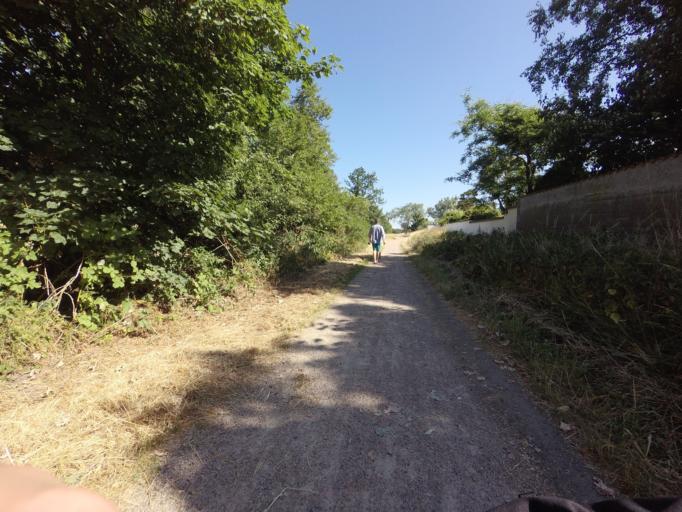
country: SE
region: Skane
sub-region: Vellinge Kommun
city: Skanor med Falsterbo
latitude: 55.3984
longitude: 12.8322
